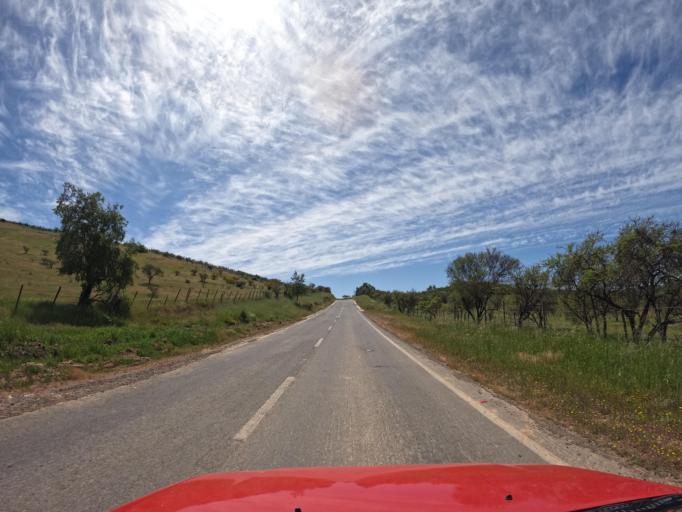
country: CL
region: Maule
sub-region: Provincia de Talca
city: Talca
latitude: -35.0188
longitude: -71.7718
